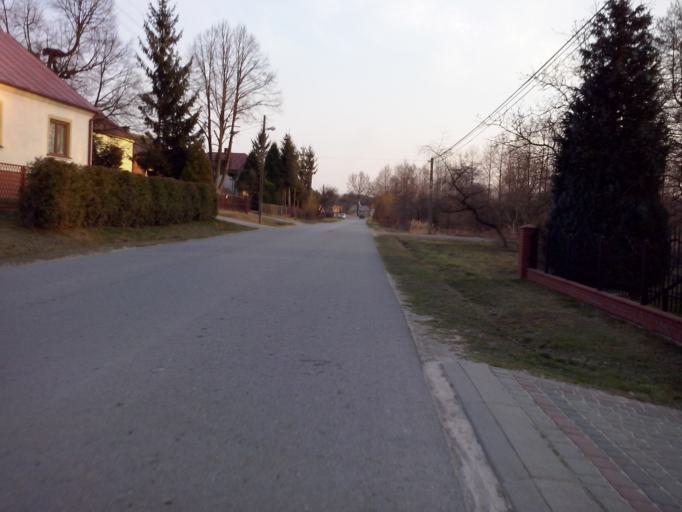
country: PL
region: Subcarpathian Voivodeship
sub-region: Powiat nizanski
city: Krzeszow
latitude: 50.3919
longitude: 22.3603
